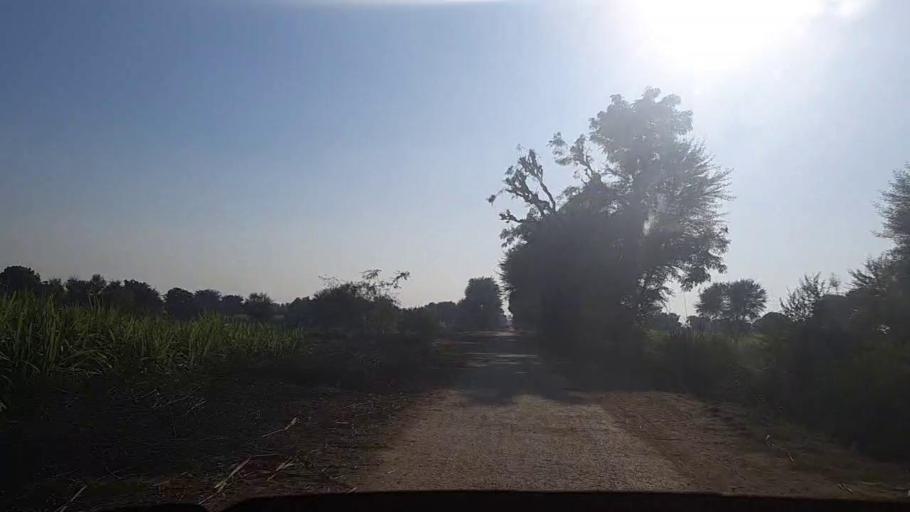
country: PK
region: Sindh
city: Gambat
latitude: 27.3512
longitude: 68.4517
